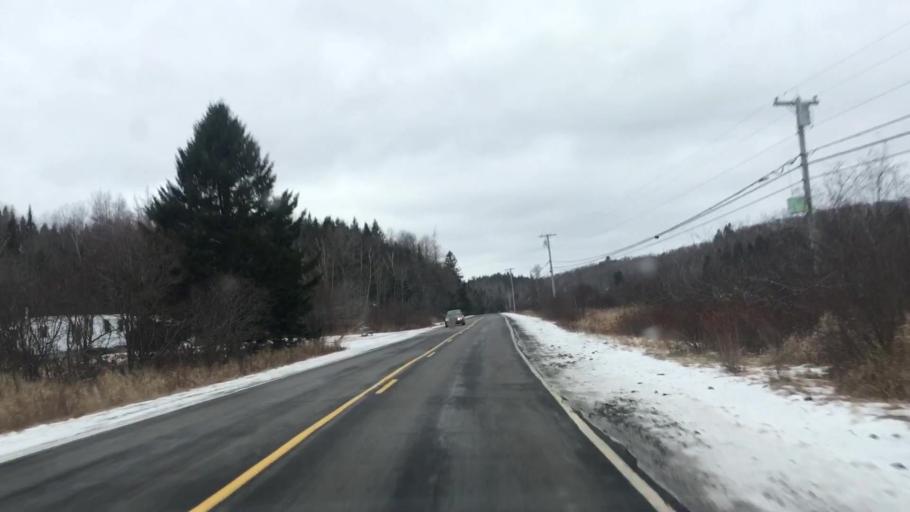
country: US
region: Maine
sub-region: Washington County
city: Machiasport
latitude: 44.7092
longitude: -67.3682
